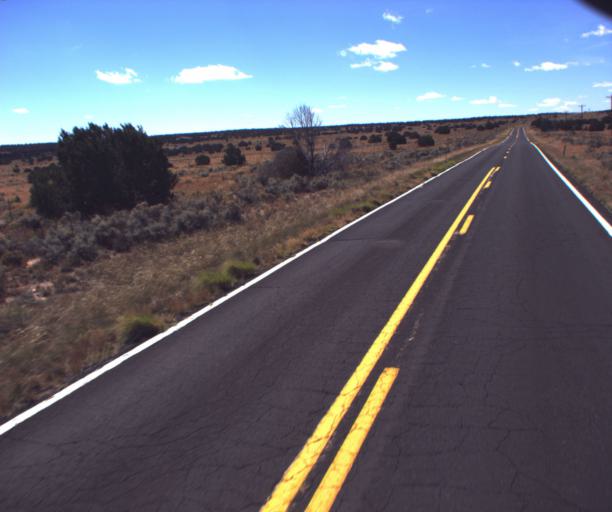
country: US
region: New Mexico
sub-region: McKinley County
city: Zuni Pueblo
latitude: 34.9797
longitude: -109.1293
